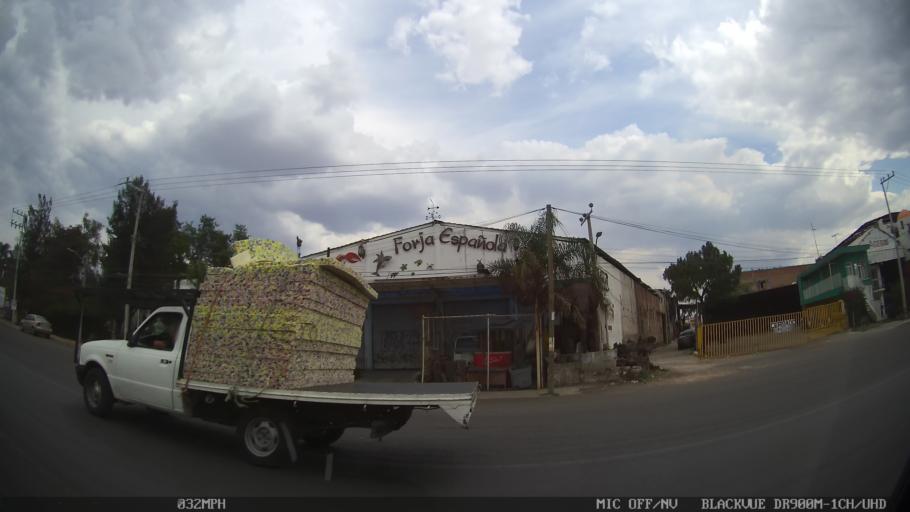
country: MX
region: Jalisco
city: Tlaquepaque
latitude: 20.6173
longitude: -103.2693
